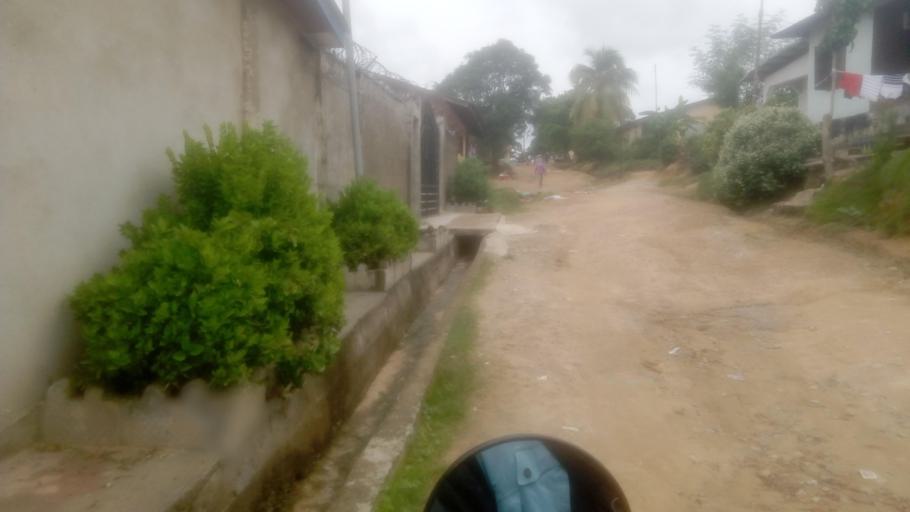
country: SL
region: Southern Province
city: Bo
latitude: 7.9432
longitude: -11.7292
